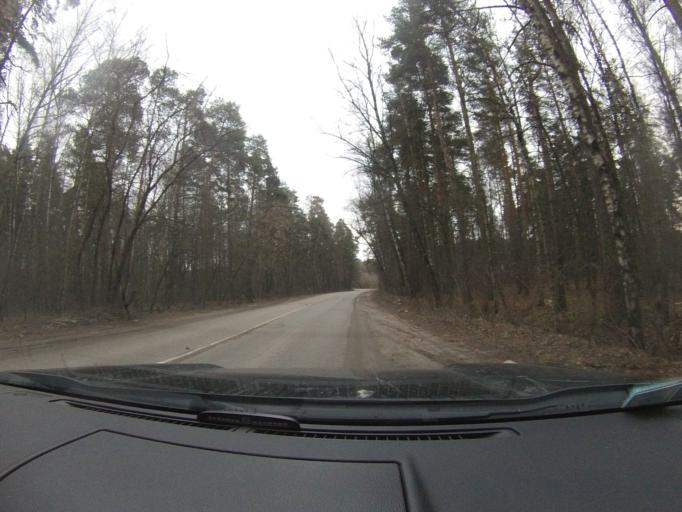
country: RU
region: Moskovskaya
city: Voskresensk
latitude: 55.3359
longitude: 38.6750
